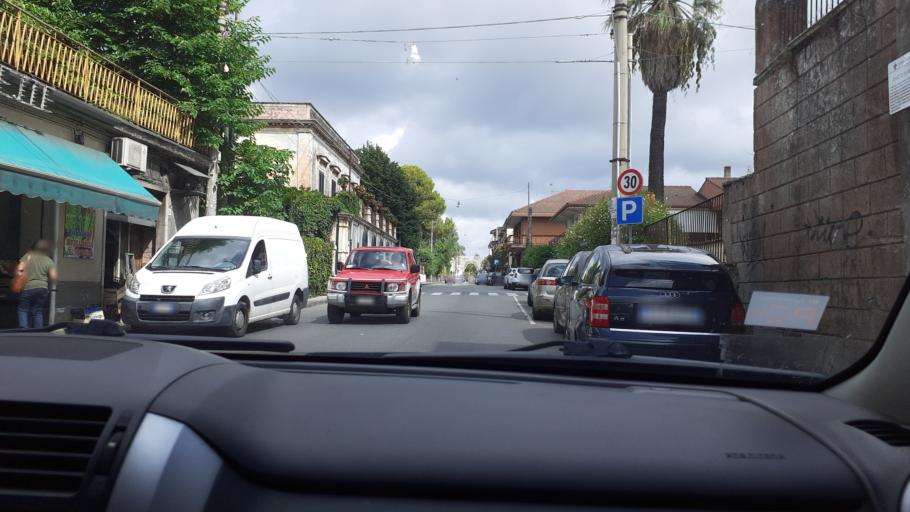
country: IT
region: Sicily
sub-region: Catania
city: San Giovanni la Punta
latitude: 37.5815
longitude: 15.0960
